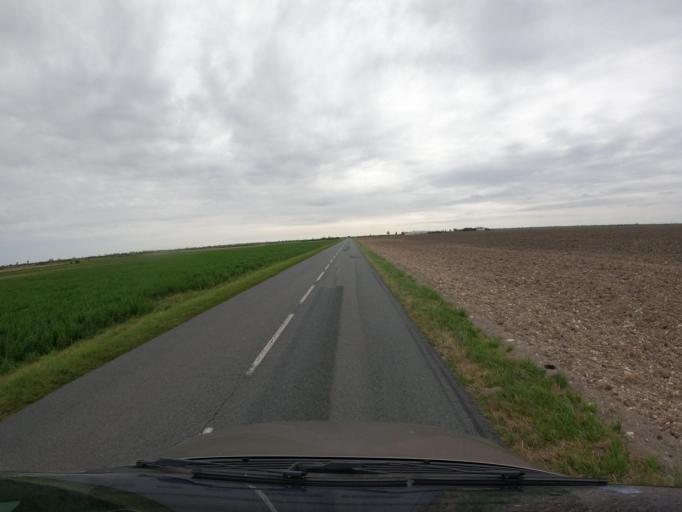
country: FR
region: Poitou-Charentes
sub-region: Departement de la Charente-Maritime
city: Charron
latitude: 46.3063
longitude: -1.0581
